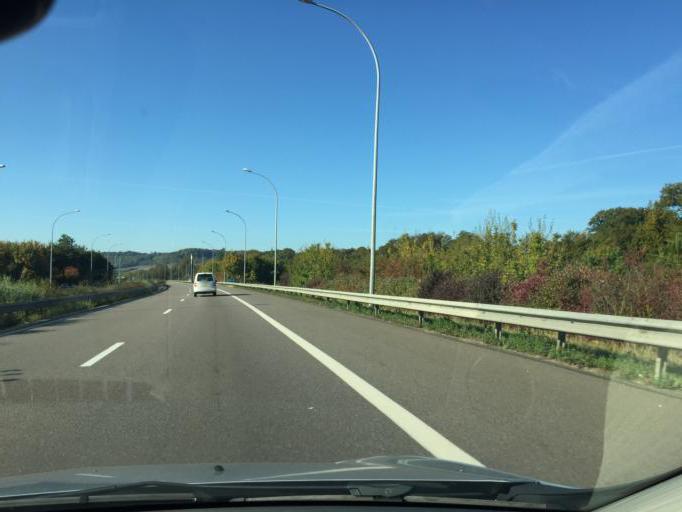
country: LU
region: Grevenmacher
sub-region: Canton de Grevenmacher
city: Flaxweiler
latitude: 49.6636
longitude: 6.3570
